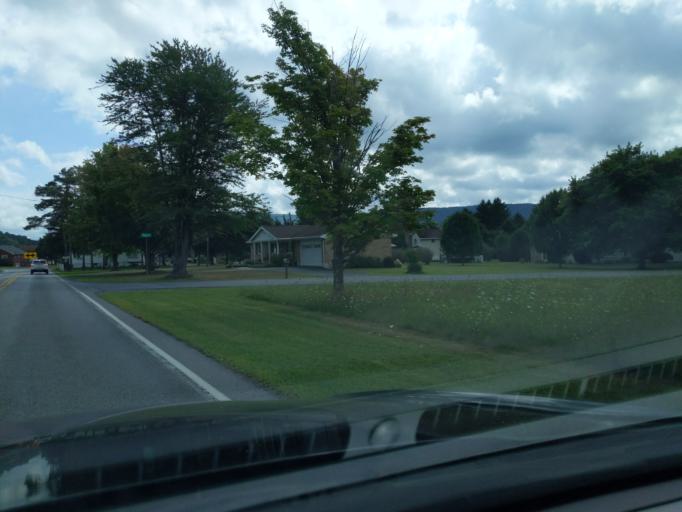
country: US
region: Pennsylvania
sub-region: Blair County
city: Duncansville
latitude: 40.3930
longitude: -78.4406
